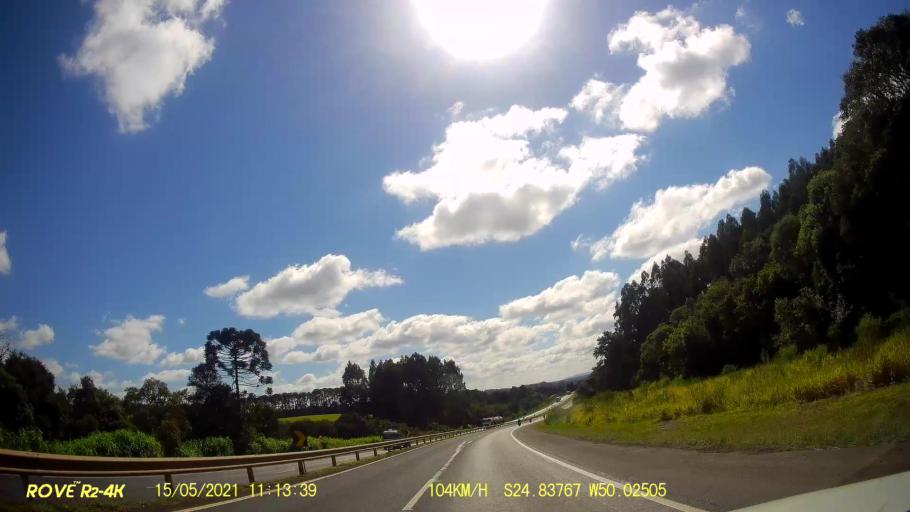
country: BR
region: Parana
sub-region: Castro
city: Castro
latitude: -24.8380
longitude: -50.0252
